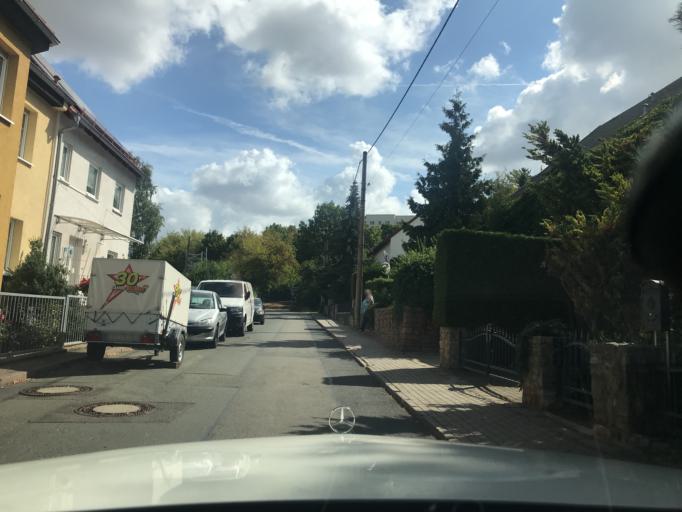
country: DE
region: Thuringia
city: Erfurt
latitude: 50.9541
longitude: 11.0655
